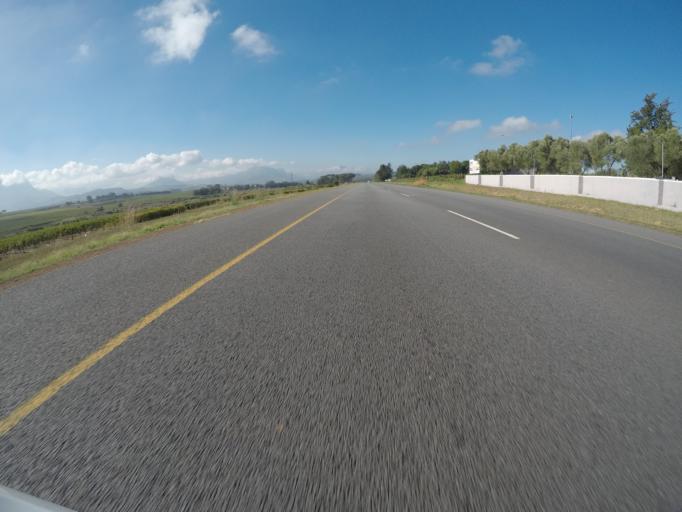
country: ZA
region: Western Cape
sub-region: Cape Winelands District Municipality
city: Stellenbosch
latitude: -33.8633
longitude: 18.8116
